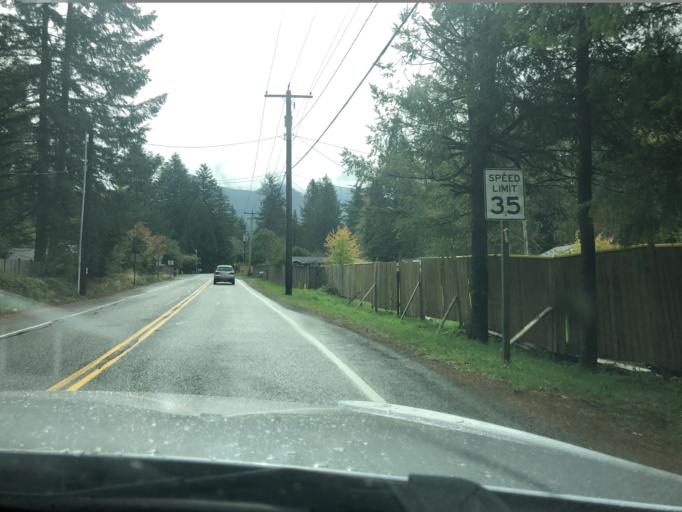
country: US
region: Washington
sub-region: King County
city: Riverbend
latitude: 47.4471
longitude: -121.7587
